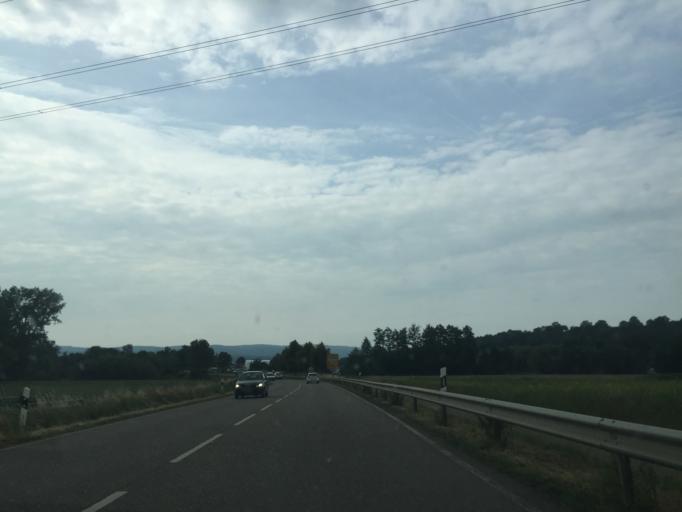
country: DE
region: Baden-Wuerttemberg
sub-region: Karlsruhe Region
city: Meckesheim
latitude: 49.3298
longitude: 8.8101
